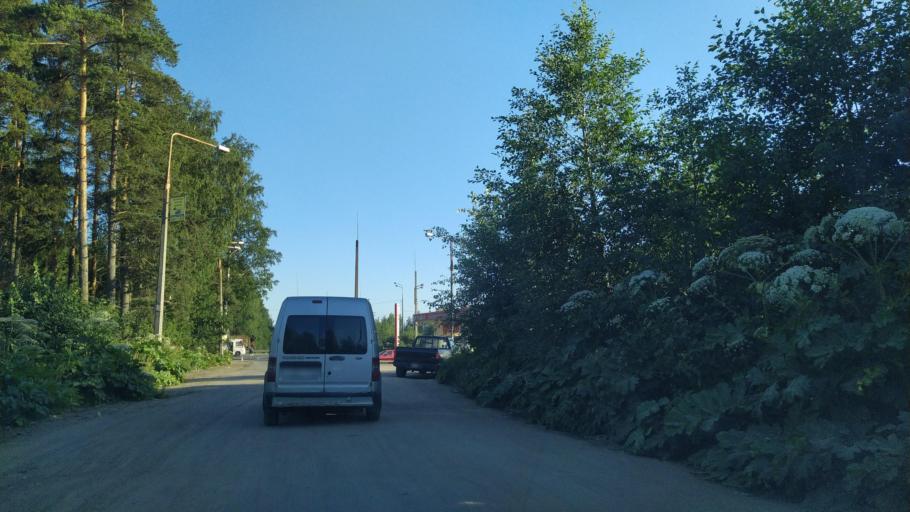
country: RU
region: Leningrad
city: Koltushi
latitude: 59.9017
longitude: 30.7334
